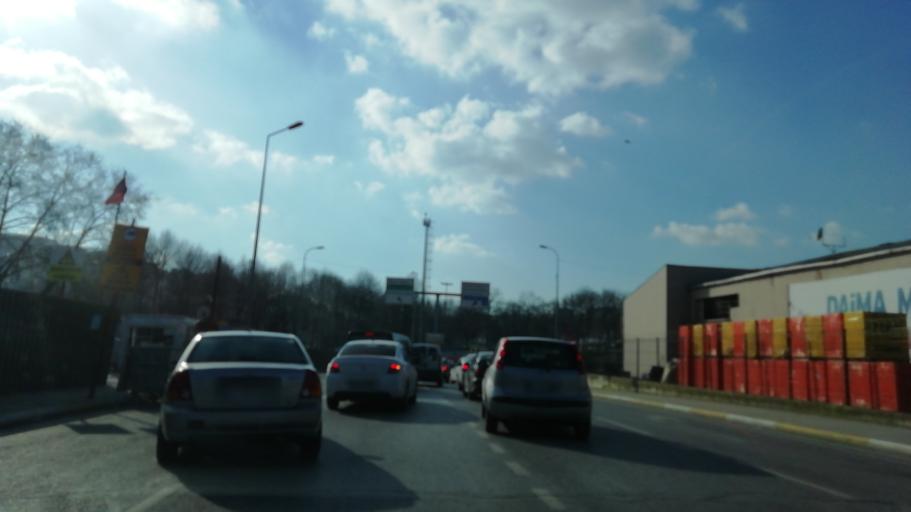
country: TR
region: Istanbul
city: Sisli
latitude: 41.0753
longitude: 28.9482
